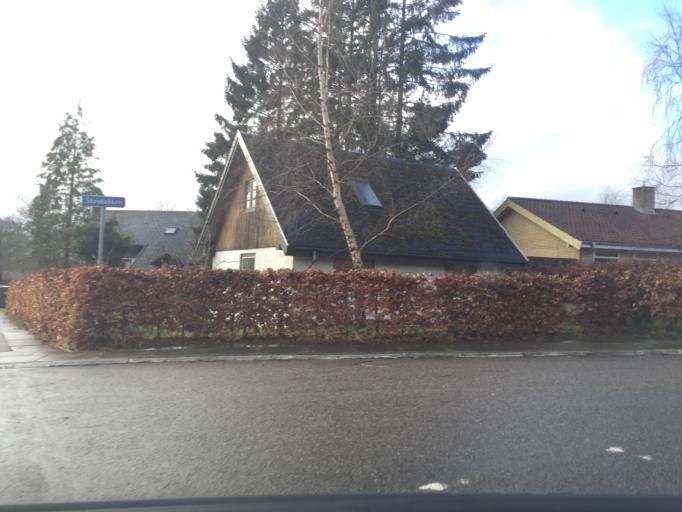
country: DK
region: Capital Region
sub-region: Fureso Kommune
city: Stavnsholt
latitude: 55.8076
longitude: 12.3945
